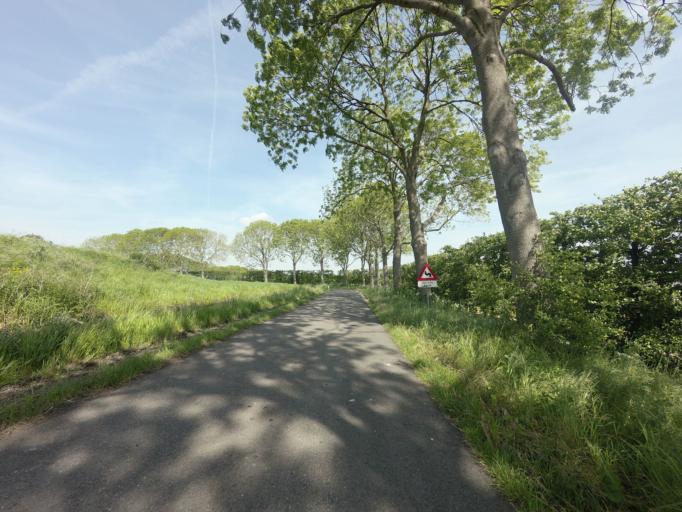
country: NL
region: Utrecht
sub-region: Gemeente De Ronde Venen
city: Mijdrecht
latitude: 52.2288
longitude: 4.8864
